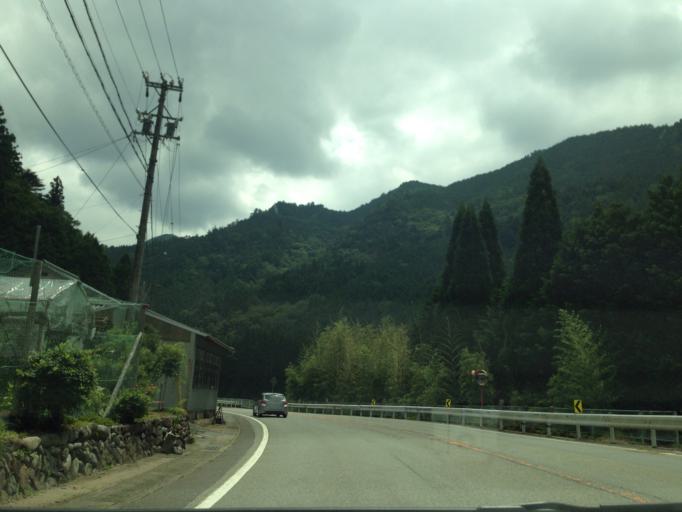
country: JP
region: Gifu
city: Gujo
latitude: 35.7489
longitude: 137.2155
